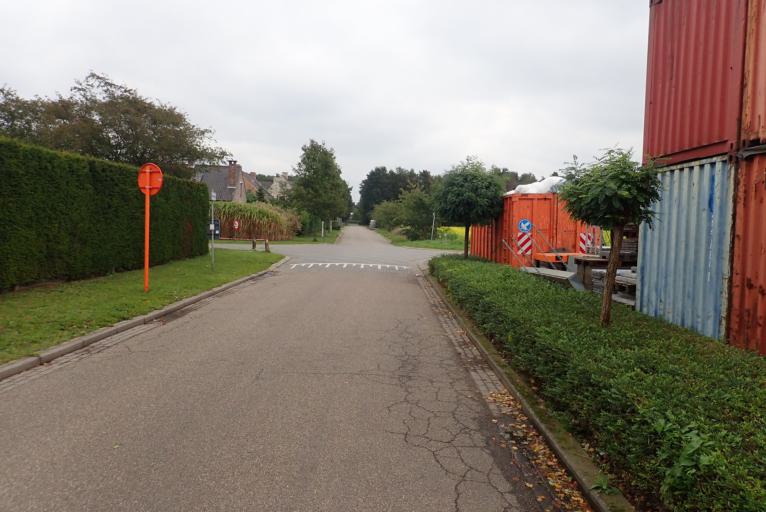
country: BE
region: Flanders
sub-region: Provincie Antwerpen
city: Zandhoven
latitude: 51.2063
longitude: 4.6476
